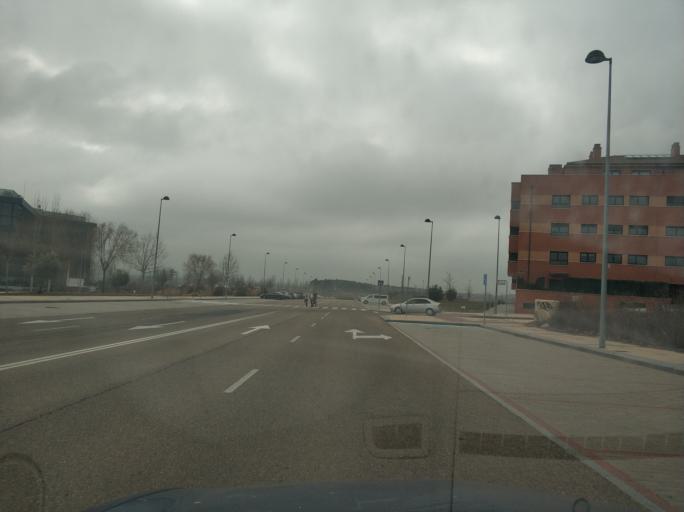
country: ES
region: Castille and Leon
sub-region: Provincia de Valladolid
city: Arroyo
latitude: 41.6167
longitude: -4.7973
